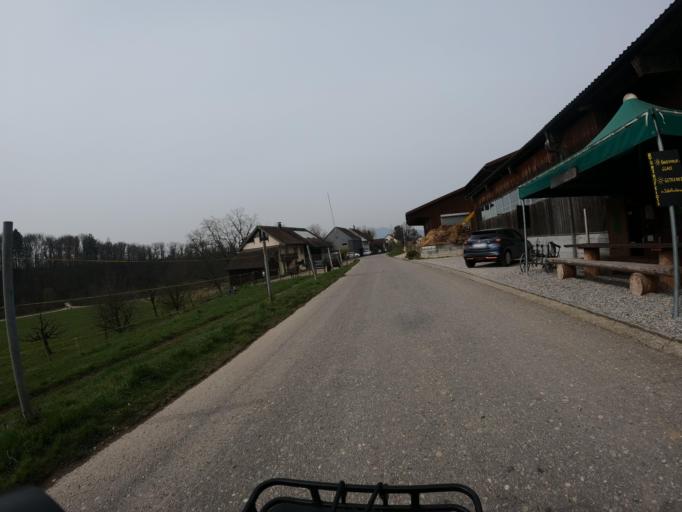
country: CH
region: Aargau
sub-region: Bezirk Lenzburg
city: Niederlenz
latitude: 47.4112
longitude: 8.1871
